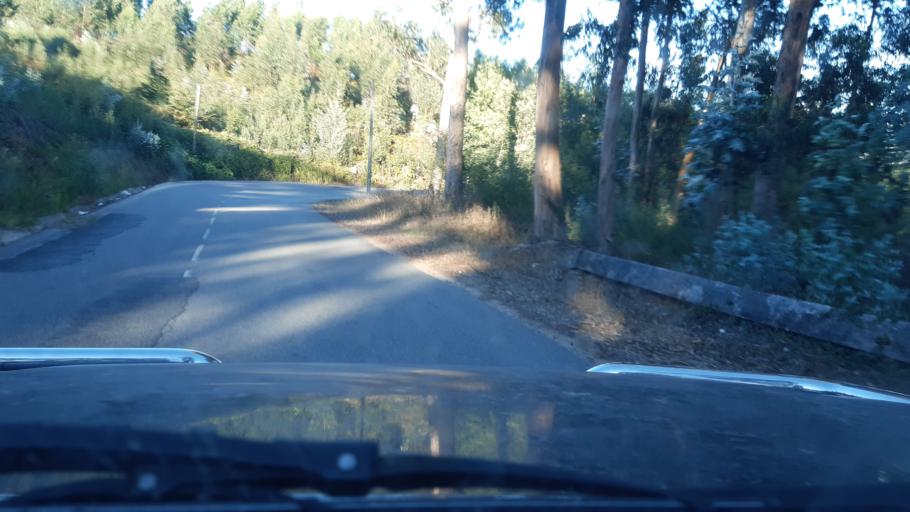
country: PT
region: Aveiro
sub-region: Agueda
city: Agueda
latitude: 40.5773
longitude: -8.4621
